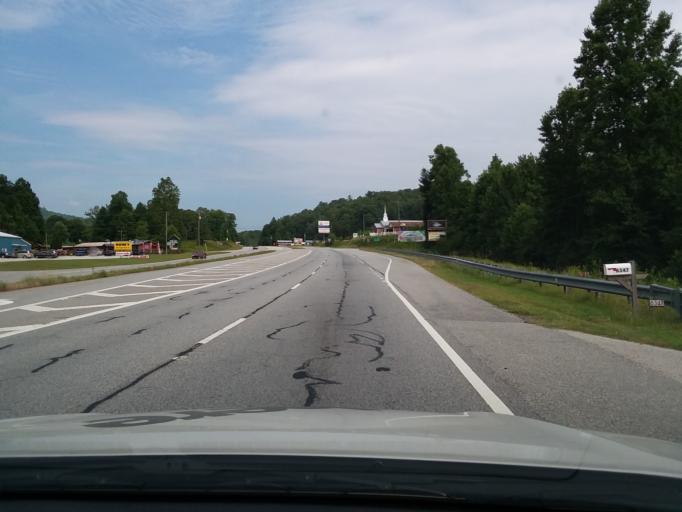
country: US
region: Georgia
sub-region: Rabun County
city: Clayton
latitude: 34.7977
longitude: -83.4177
